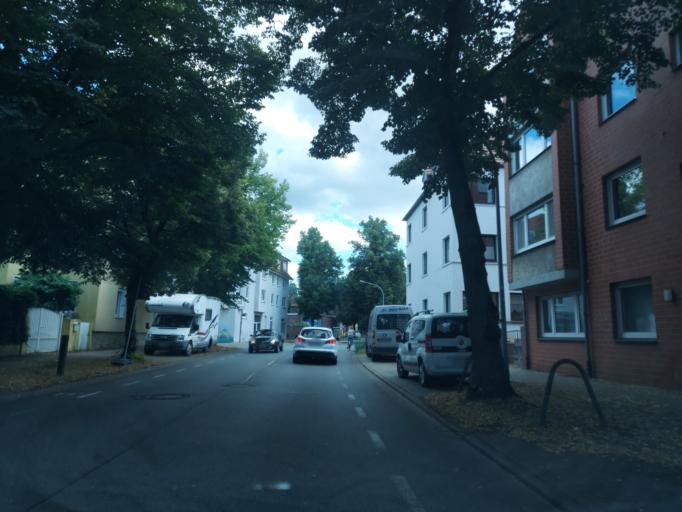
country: DE
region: Lower Saxony
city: Osnabrueck
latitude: 52.2643
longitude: 8.0438
